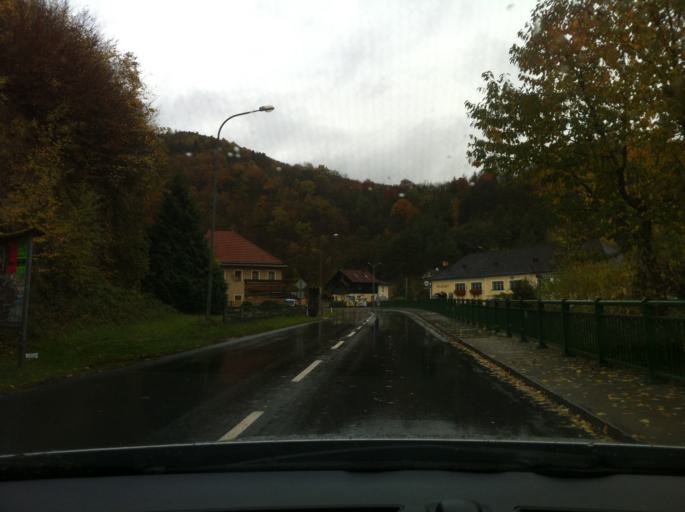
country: AT
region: Lower Austria
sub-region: Politischer Bezirk Melk
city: Weiten
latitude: 48.3034
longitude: 15.2568
